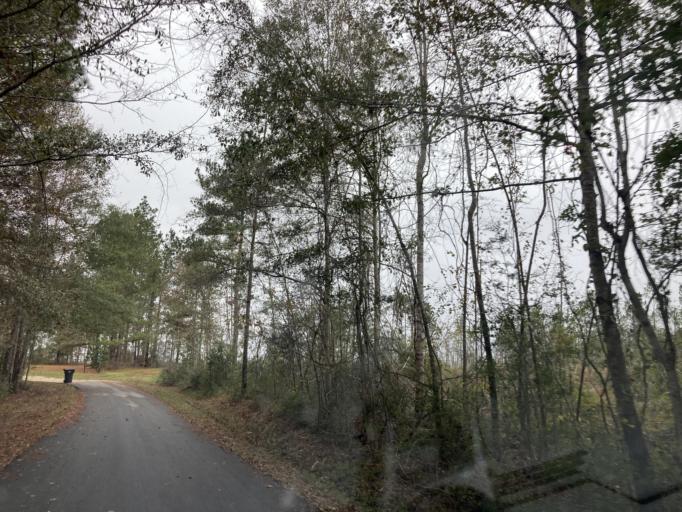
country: US
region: Mississippi
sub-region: Lamar County
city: Purvis
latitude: 31.2320
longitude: -89.5057
